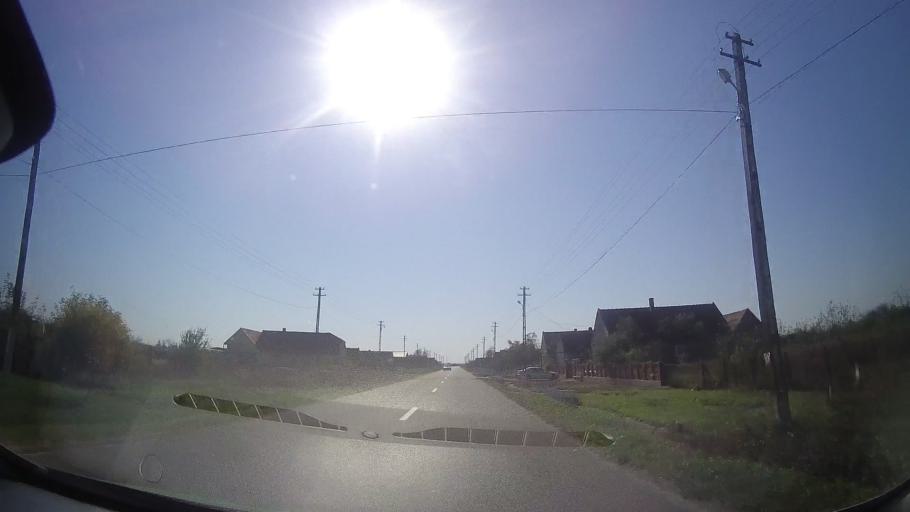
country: RO
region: Timis
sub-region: Comuna Ghizela
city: Ghizela
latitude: 45.7931
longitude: 21.7288
